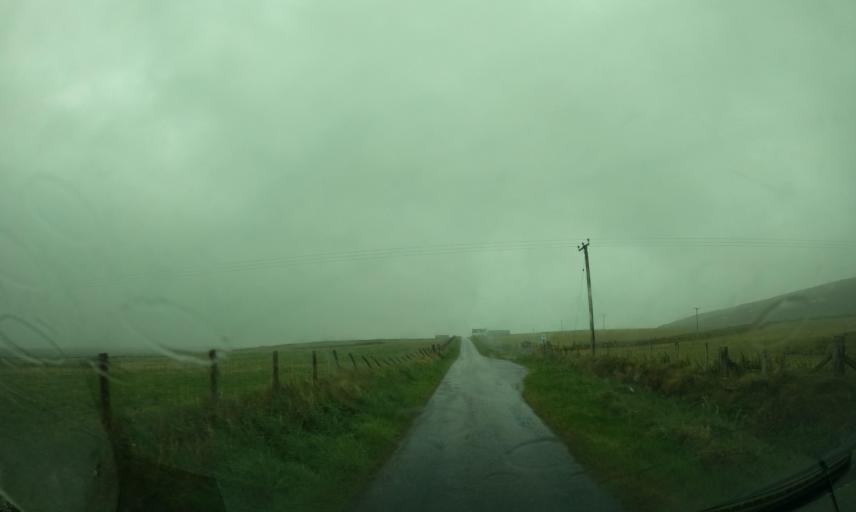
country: GB
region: Scotland
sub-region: Eilean Siar
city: Barra
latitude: 56.4600
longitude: -6.9337
